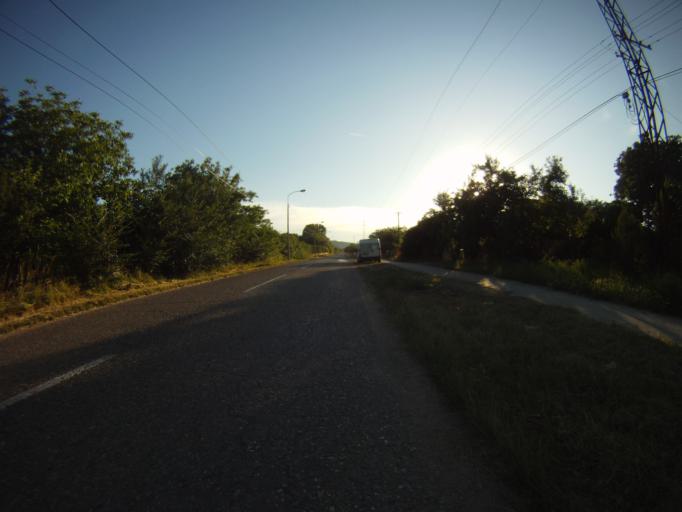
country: RS
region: Central Serbia
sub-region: Nisavski Okrug
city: Niska Banja
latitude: 43.3003
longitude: 22.0128
